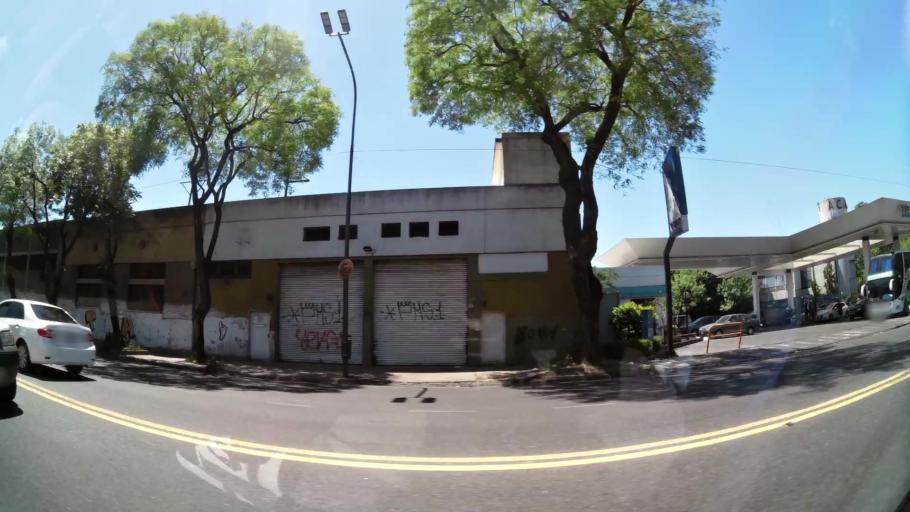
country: AR
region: Buenos Aires
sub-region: Partido de Avellaneda
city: Avellaneda
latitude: -34.6447
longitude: -58.3895
